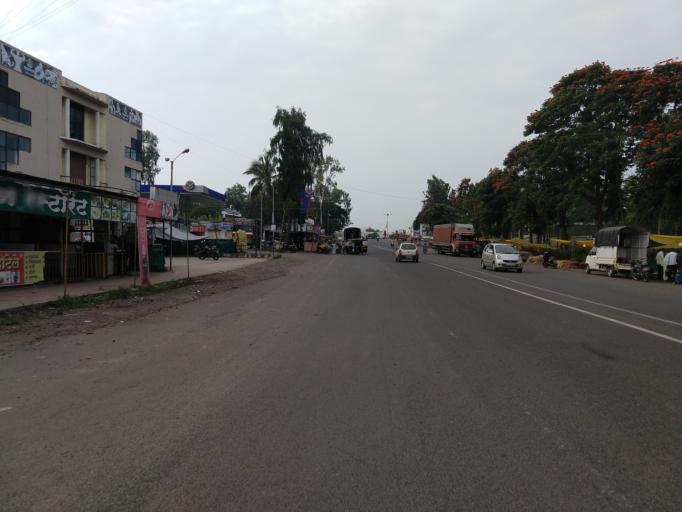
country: IN
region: Maharashtra
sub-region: Pune Division
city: Sasvad
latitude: 18.3494
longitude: 74.0288
